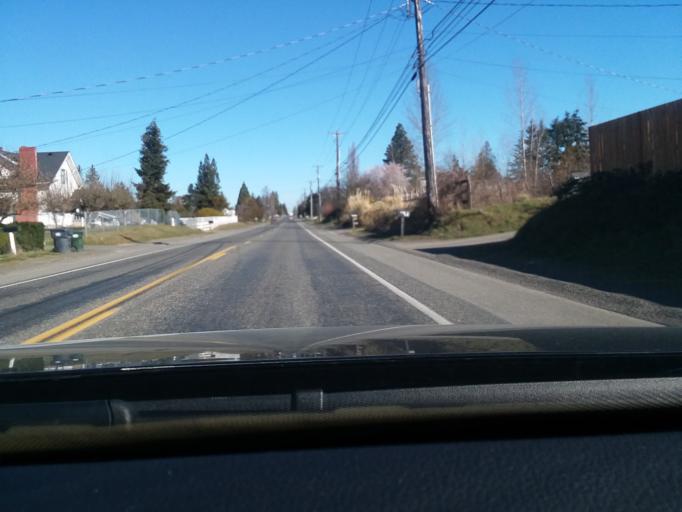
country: US
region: Washington
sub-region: Pierce County
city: Midland
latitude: 47.1633
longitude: -122.3889
